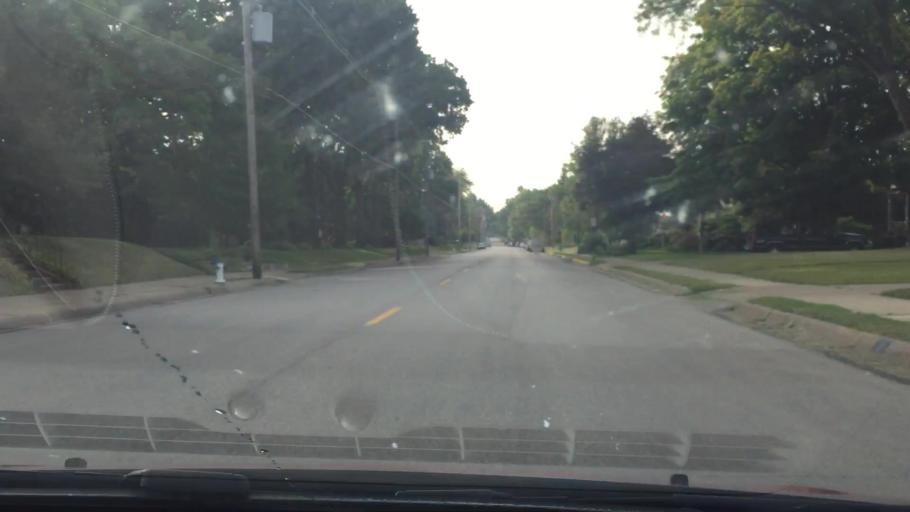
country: US
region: Iowa
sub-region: Muscatine County
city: Muscatine
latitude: 41.4378
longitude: -91.0568
